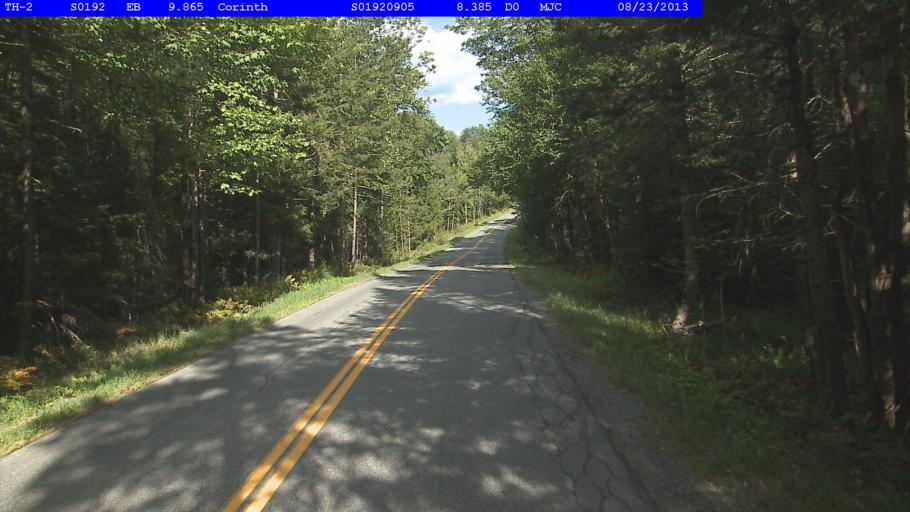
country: US
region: New Hampshire
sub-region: Grafton County
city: Orford
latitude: 44.0217
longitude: -72.2181
